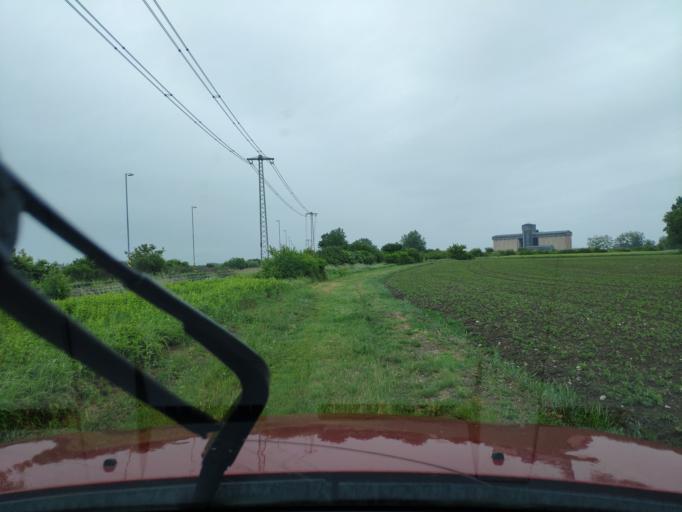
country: SK
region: Kosicky
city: Cierna nad Tisou
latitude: 48.4182
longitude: 22.0386
